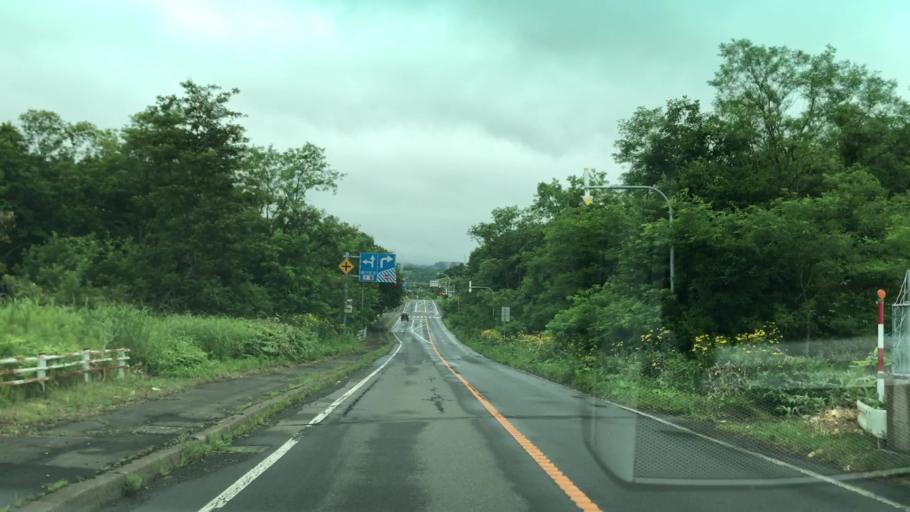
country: JP
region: Hokkaido
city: Muroran
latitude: 42.3856
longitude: 140.9833
